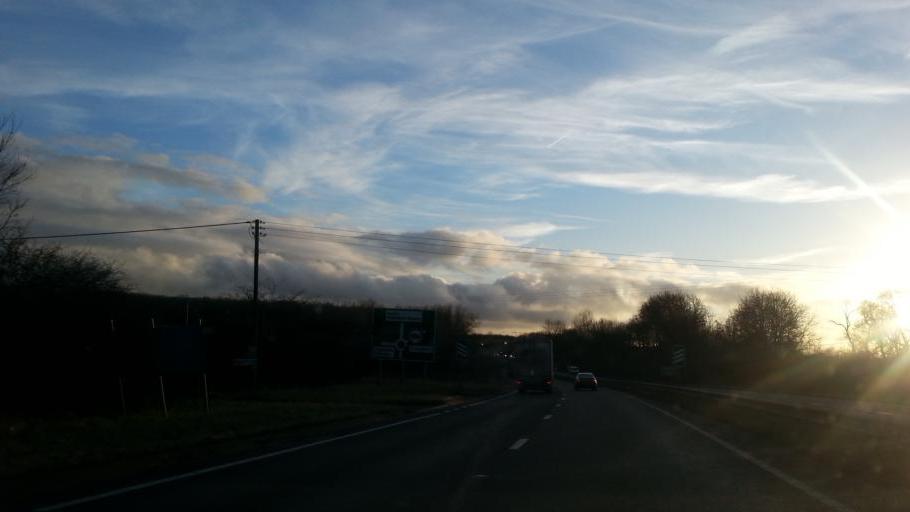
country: GB
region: England
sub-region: Northamptonshire
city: Brackley
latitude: 51.9996
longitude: -1.1602
